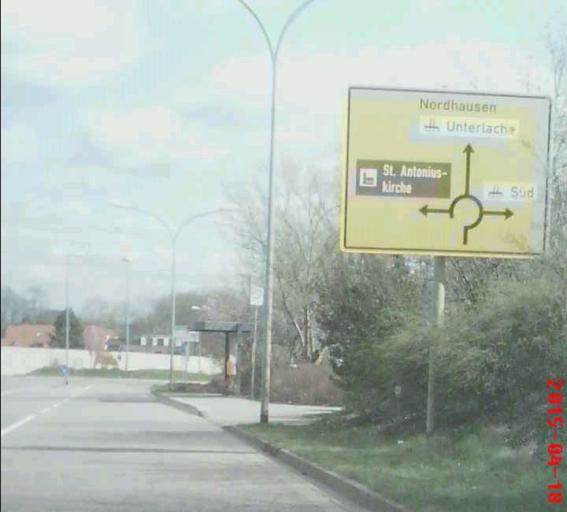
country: DE
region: Thuringia
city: Worbis
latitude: 51.4180
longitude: 10.3641
